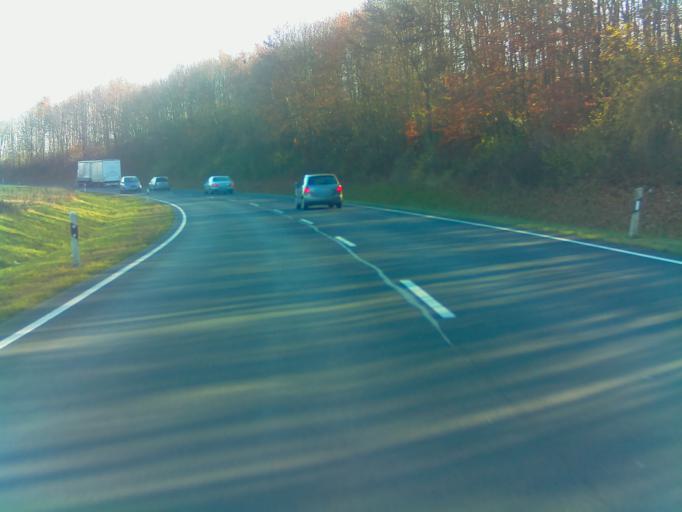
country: DE
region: Bavaria
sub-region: Regierungsbezirk Unterfranken
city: Wuelfershausen
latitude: 50.3282
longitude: 10.3226
